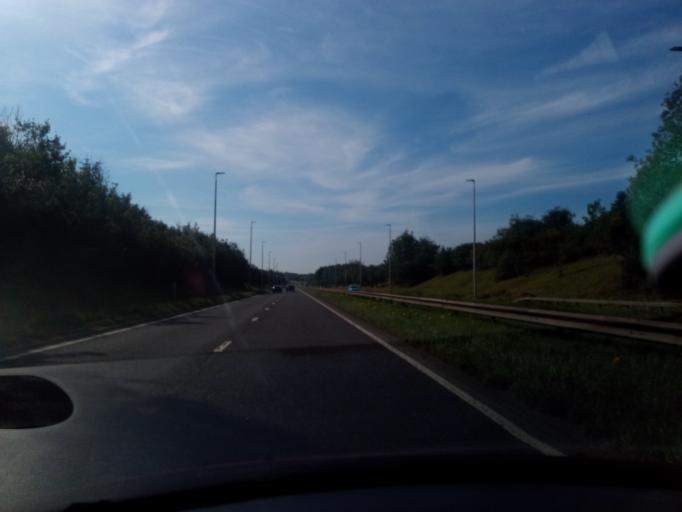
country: GB
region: England
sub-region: County Durham
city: Shotton
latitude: 54.7748
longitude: -1.3582
